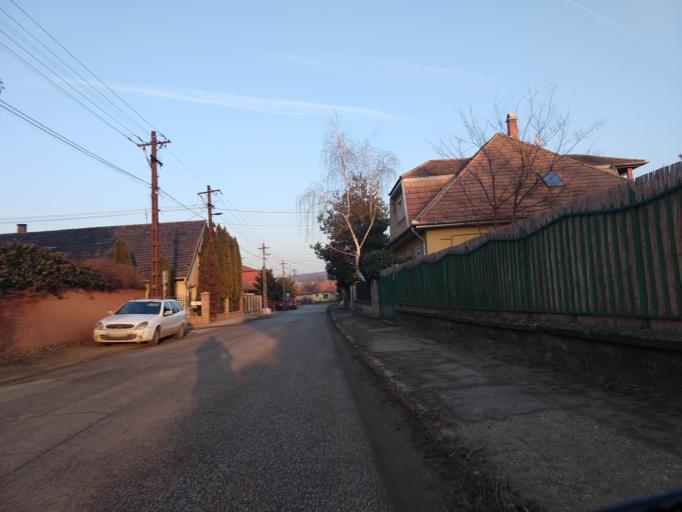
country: HU
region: Pest
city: Veresegyhaz
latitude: 47.6468
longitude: 19.2836
